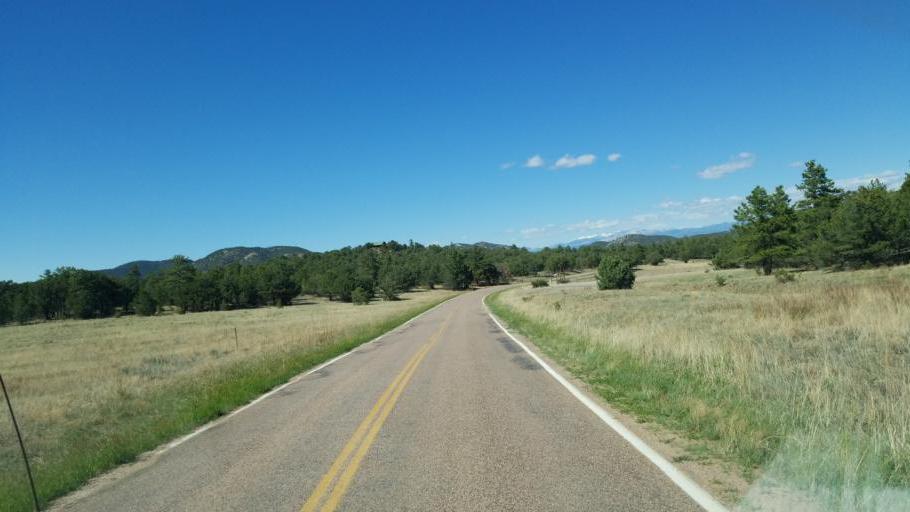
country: US
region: Colorado
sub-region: Custer County
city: Westcliffe
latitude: 38.3428
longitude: -105.4846
